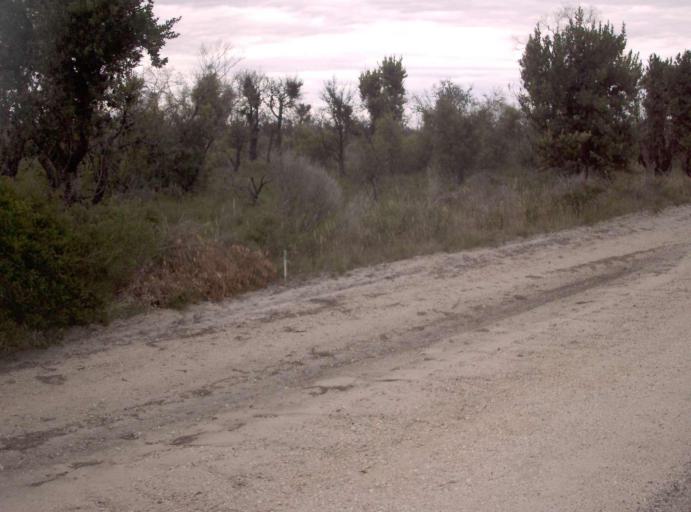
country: AU
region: Victoria
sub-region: East Gippsland
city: Bairnsdale
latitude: -38.1245
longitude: 147.4500
